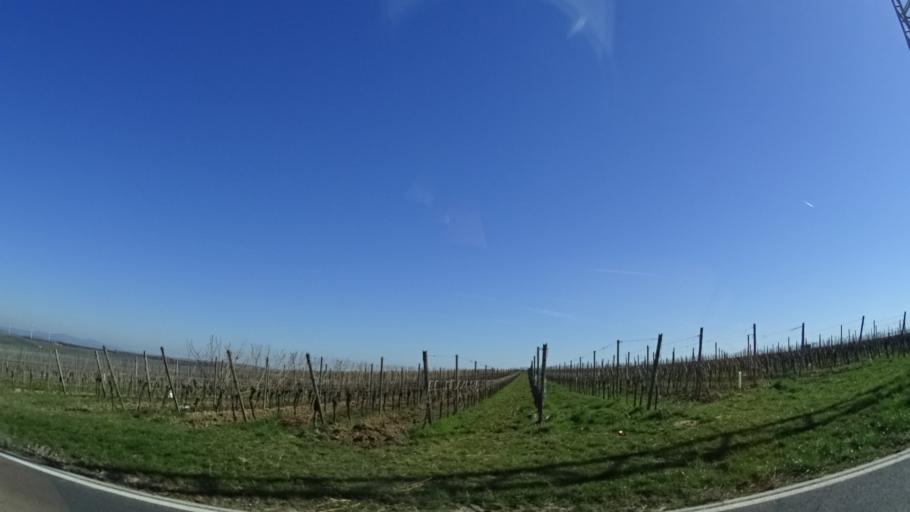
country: DE
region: Rheinland-Pfalz
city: Weinolsheim
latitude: 49.8250
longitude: 8.2651
